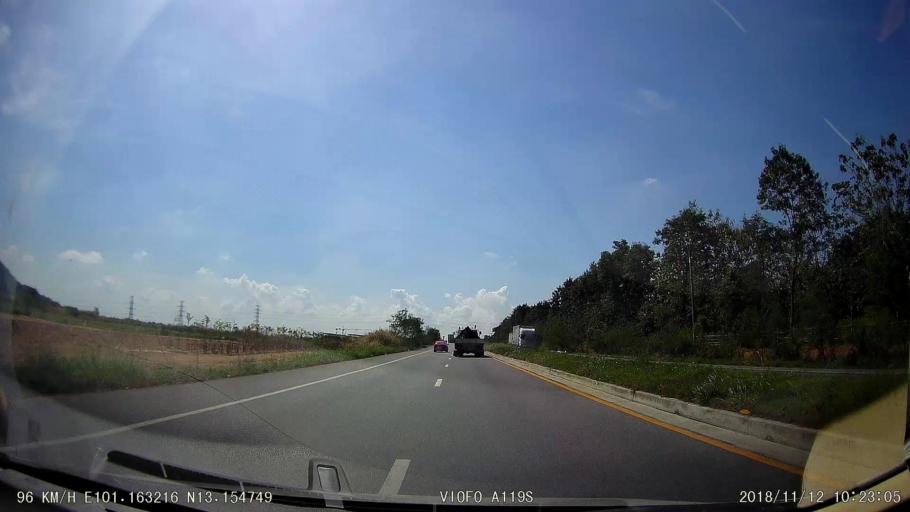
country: TH
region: Chon Buri
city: Ban Bueng
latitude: 13.1544
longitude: 101.1632
